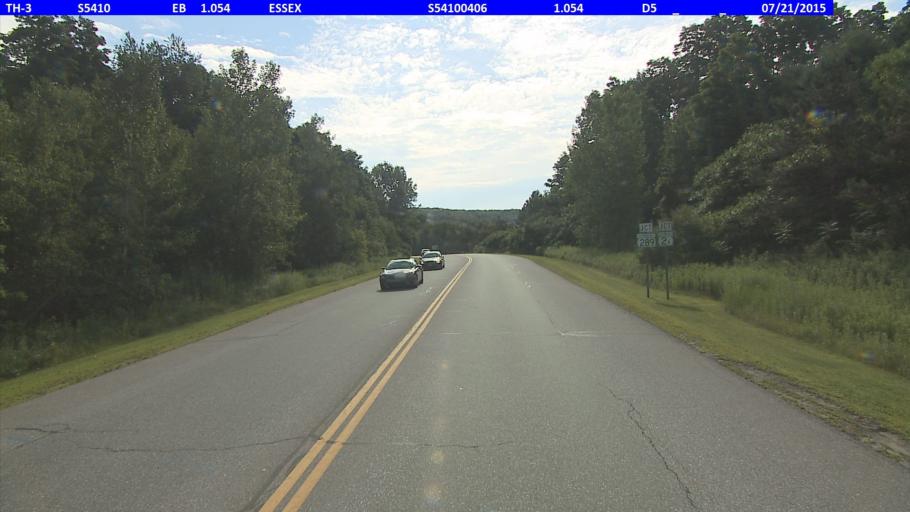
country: US
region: Vermont
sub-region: Chittenden County
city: Essex Junction
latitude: 44.5150
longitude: -73.1263
